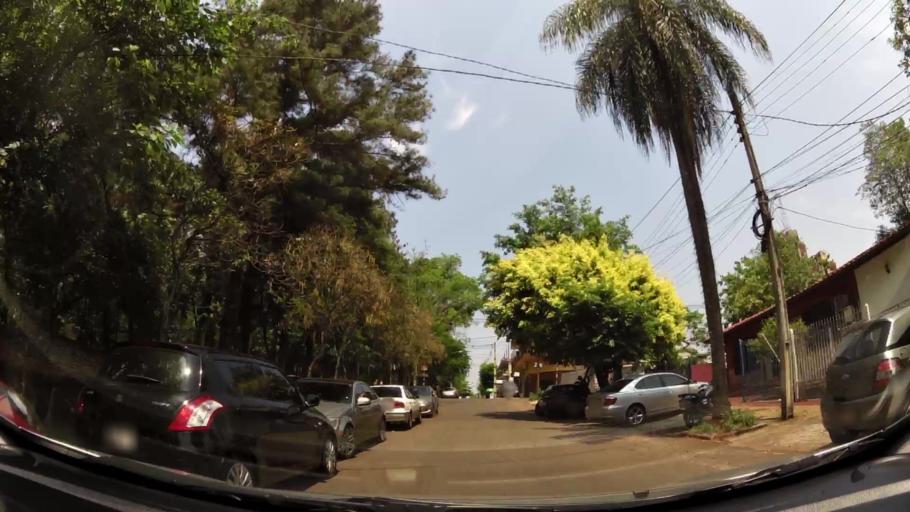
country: PY
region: Alto Parana
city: Ciudad del Este
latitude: -25.5152
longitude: -54.6118
